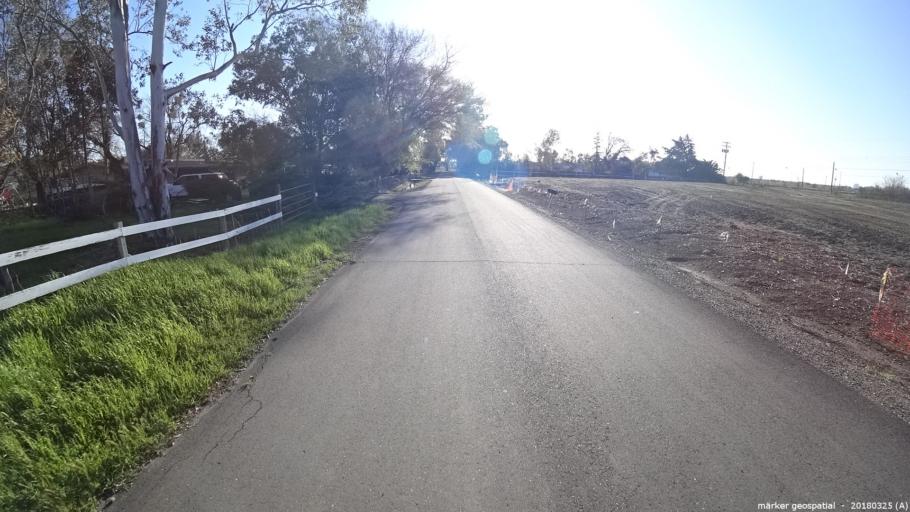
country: US
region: California
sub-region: Yolo County
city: West Sacramento
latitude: 38.6360
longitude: -121.5393
